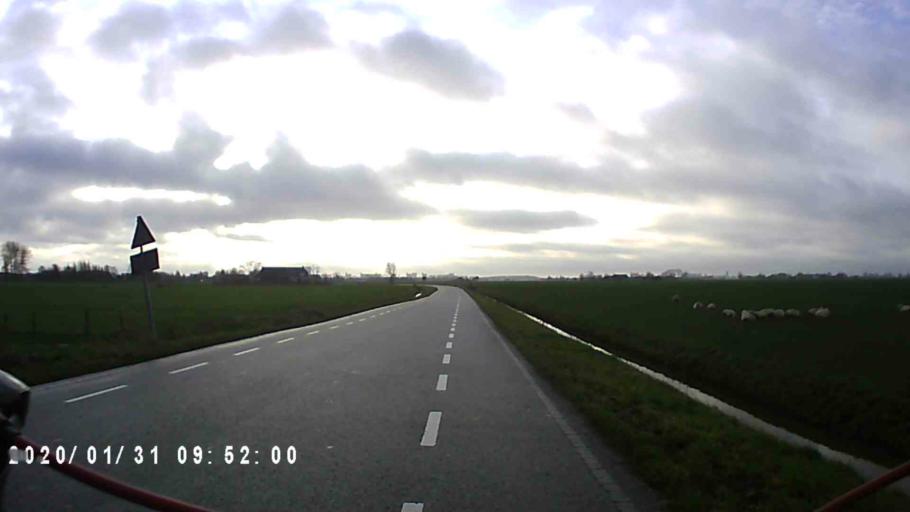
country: NL
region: Groningen
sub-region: Gemeente Zuidhorn
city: Aduard
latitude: 53.2565
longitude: 6.5023
